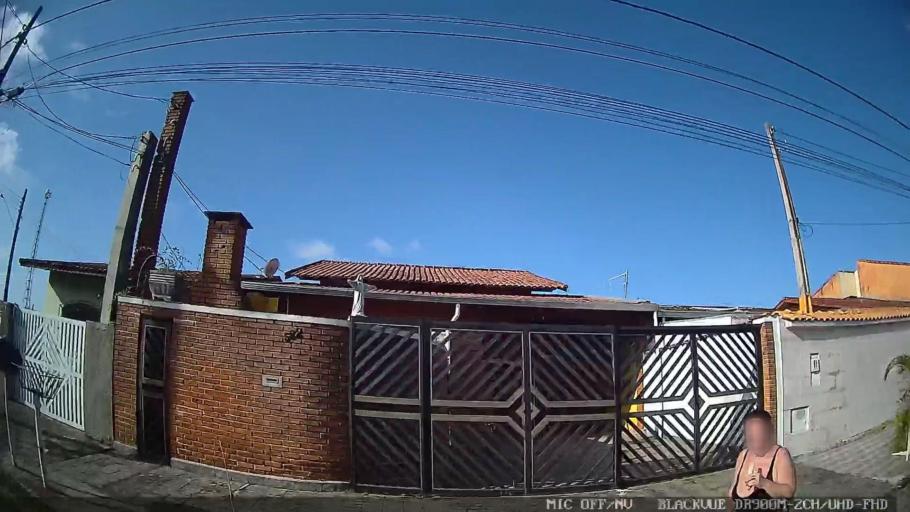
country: BR
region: Sao Paulo
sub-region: Peruibe
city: Peruibe
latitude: -24.2874
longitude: -46.9671
